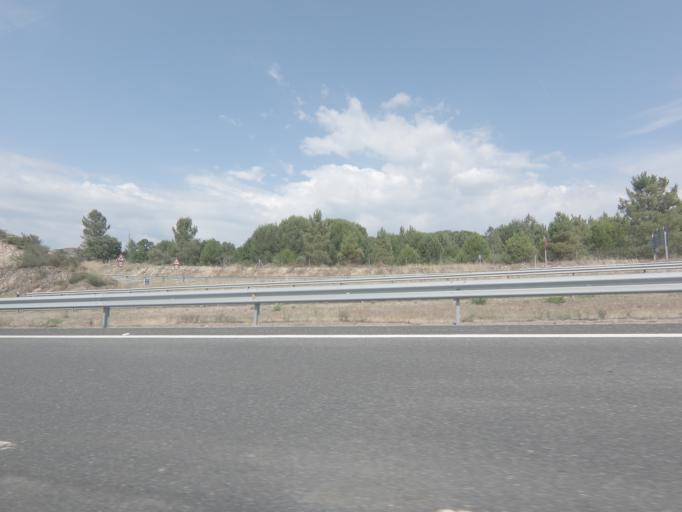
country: ES
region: Galicia
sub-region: Provincia de Ourense
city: Ourense
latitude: 42.3045
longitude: -7.8750
